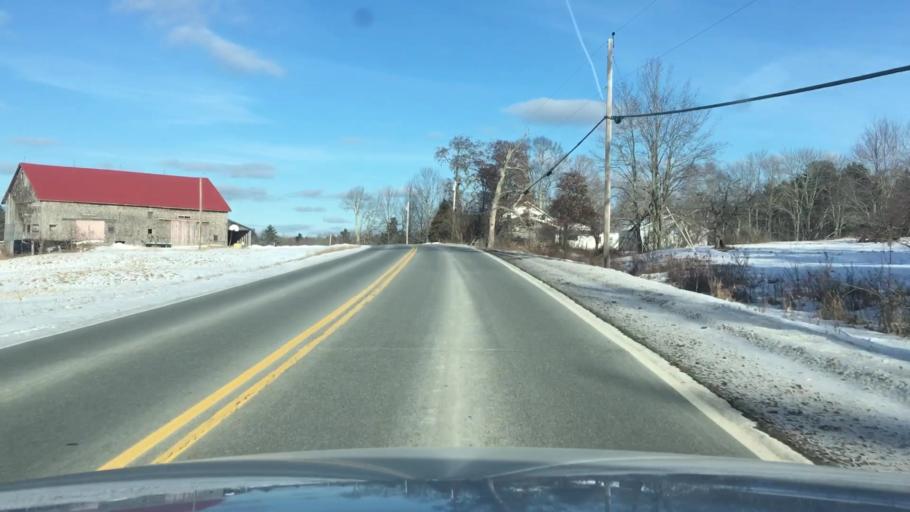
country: US
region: Maine
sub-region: Penobscot County
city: Holden
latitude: 44.7559
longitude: -68.5977
